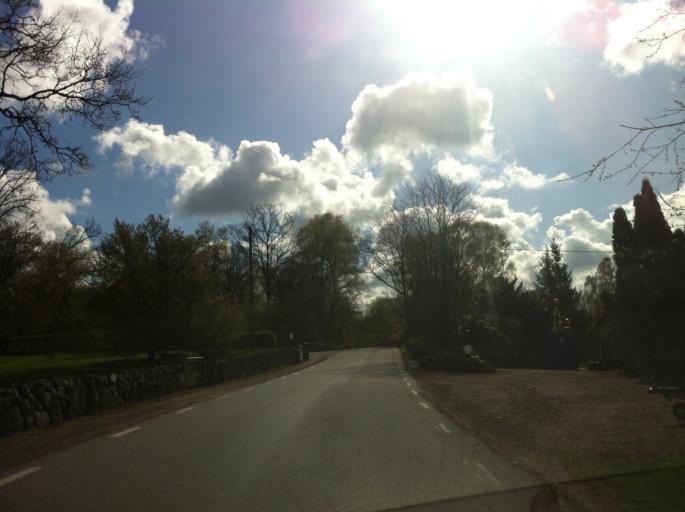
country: SE
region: Skane
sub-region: Hoors Kommun
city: Hoeoer
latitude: 55.9052
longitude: 13.5024
